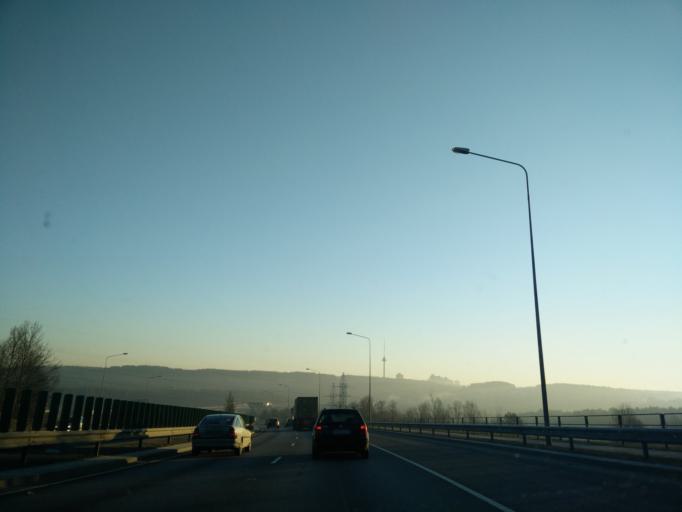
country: LT
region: Vilnius County
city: Lazdynai
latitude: 54.6629
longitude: 25.1711
